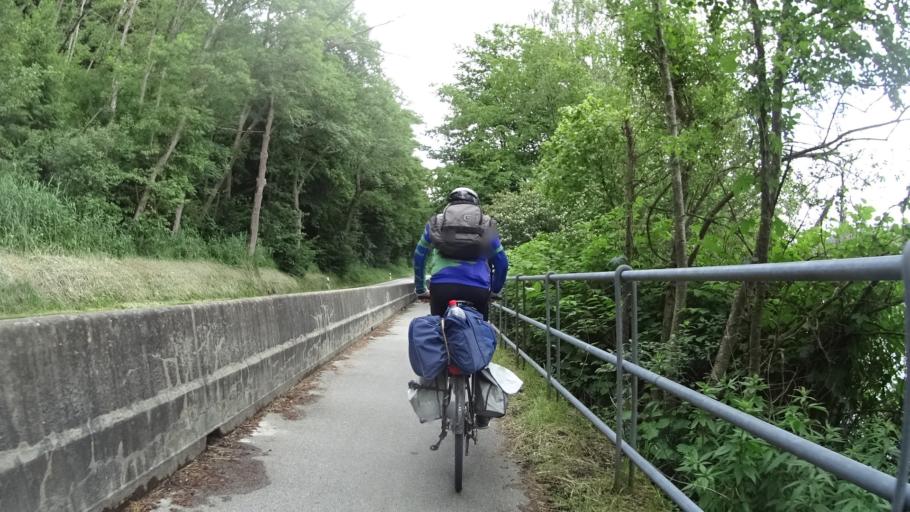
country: DE
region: Bavaria
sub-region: Lower Bavaria
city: Aicha vorm Wald
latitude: 48.6121
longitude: 13.2900
